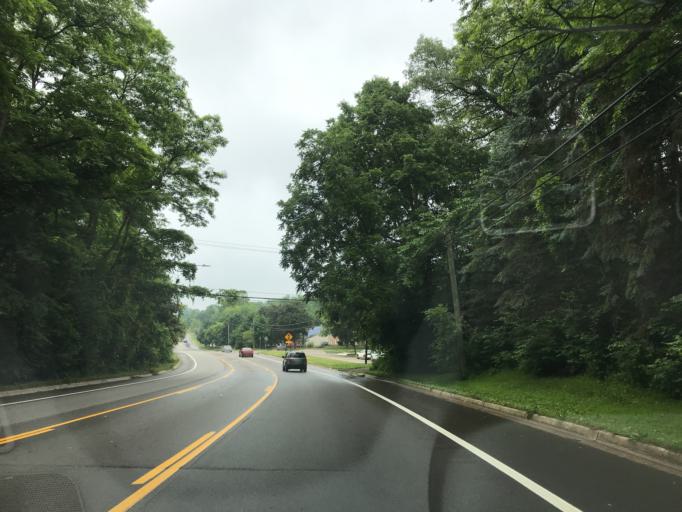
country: US
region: Michigan
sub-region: Washtenaw County
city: Ypsilanti
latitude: 42.2584
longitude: -83.6426
